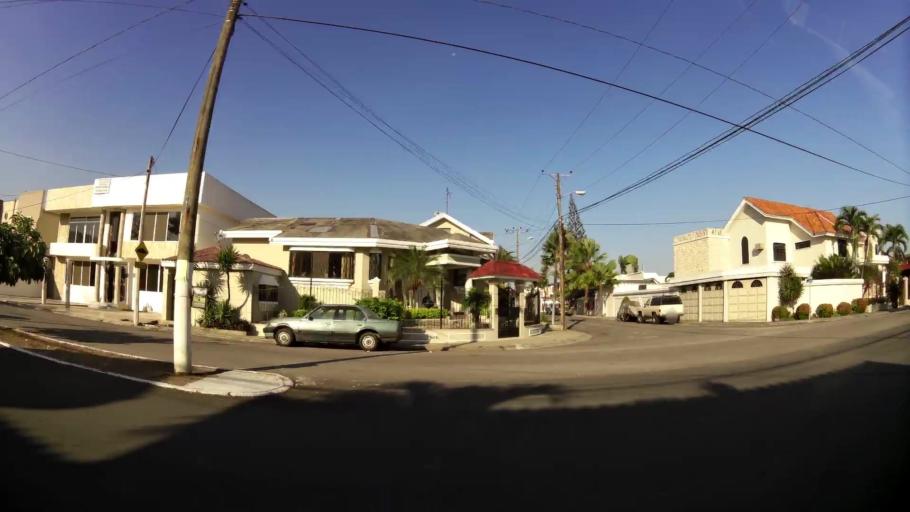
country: EC
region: Guayas
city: Santa Lucia
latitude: -2.1905
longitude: -79.9718
